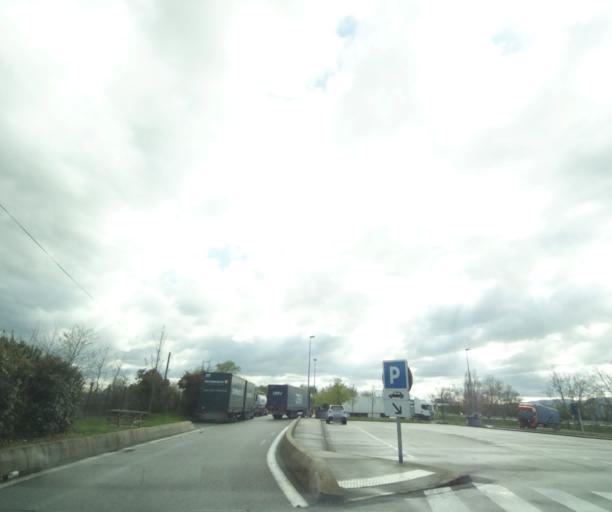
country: FR
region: Rhone-Alpes
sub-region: Departement de l'Isere
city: Auberives-sur-Vareze
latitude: 45.4097
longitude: 4.8236
